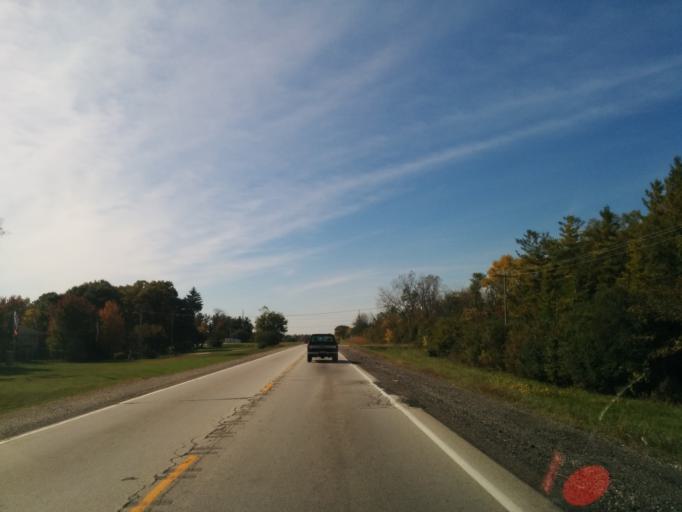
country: US
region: Illinois
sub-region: Kane County
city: Batavia
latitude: 41.8158
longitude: -88.2611
